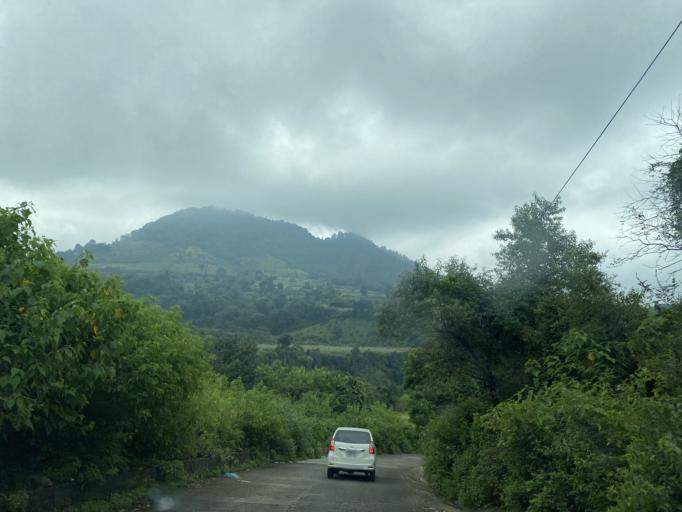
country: MX
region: Morelos
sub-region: Yecapixtla
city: Achichipico
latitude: 18.9566
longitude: -98.8263
